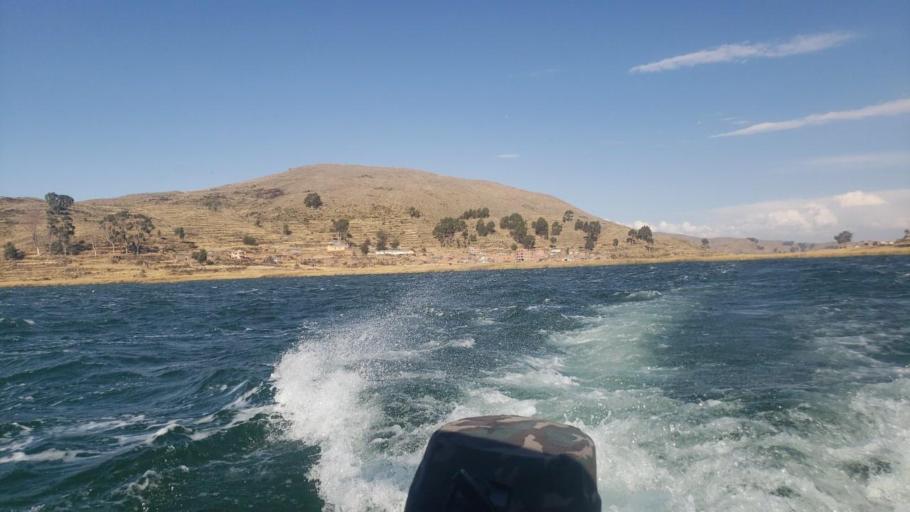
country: BO
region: La Paz
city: Huatajata
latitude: -16.3270
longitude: -68.7227
